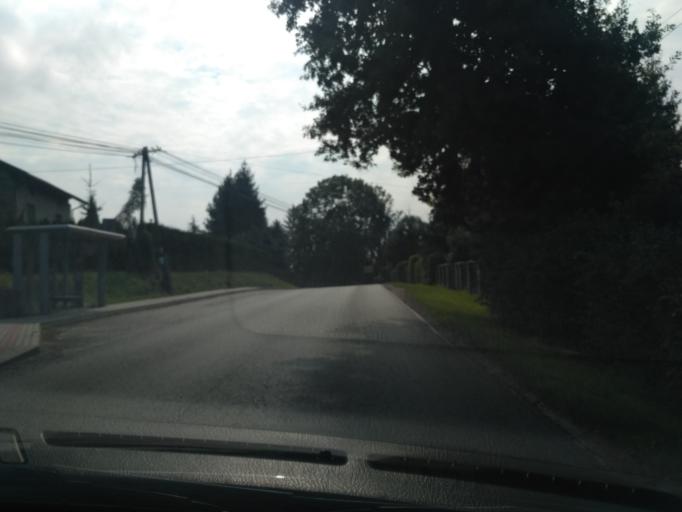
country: PL
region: Subcarpathian Voivodeship
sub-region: Powiat rzeszowski
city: Kielanowka
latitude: 50.0021
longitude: 21.9162
